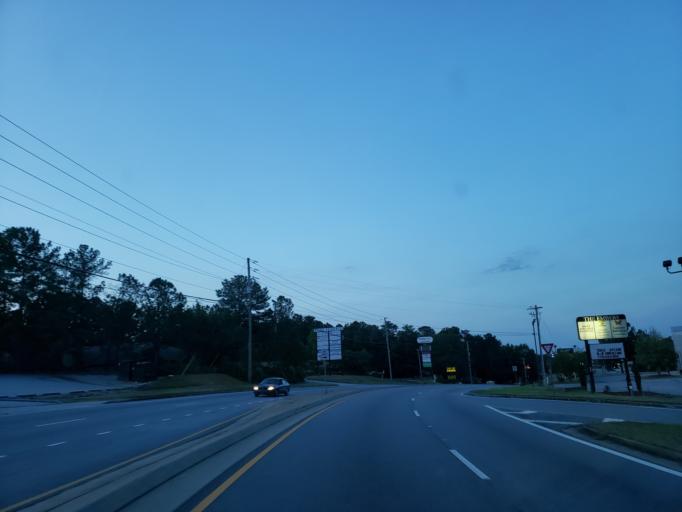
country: US
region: Georgia
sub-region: Douglas County
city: Douglasville
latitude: 33.7135
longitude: -84.7697
